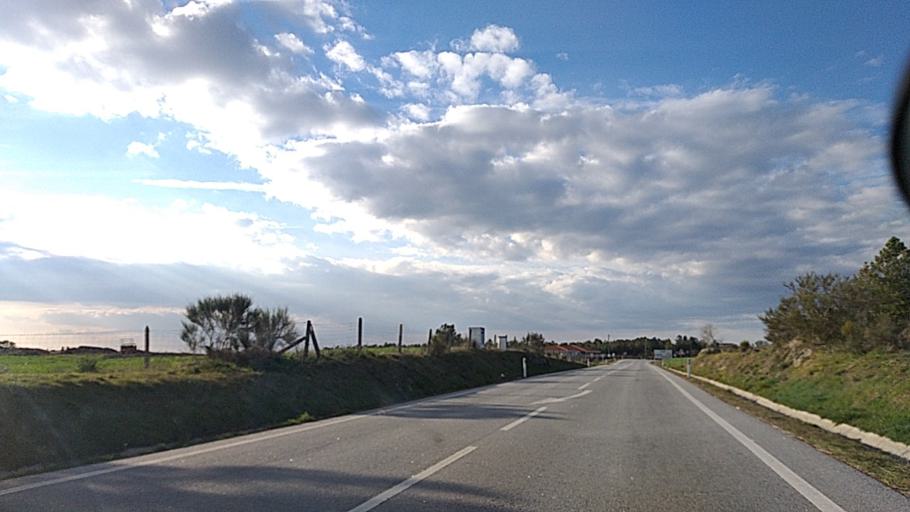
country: ES
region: Castille and Leon
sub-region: Provincia de Salamanca
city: Aldea del Obispo
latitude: 40.6709
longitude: -6.8606
